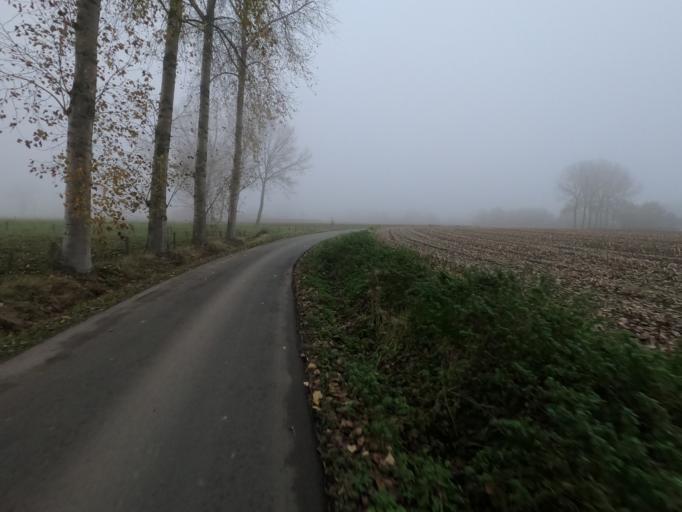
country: BE
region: Flanders
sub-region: Provincie Oost-Vlaanderen
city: Kruibeke
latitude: 51.1791
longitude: 4.2960
